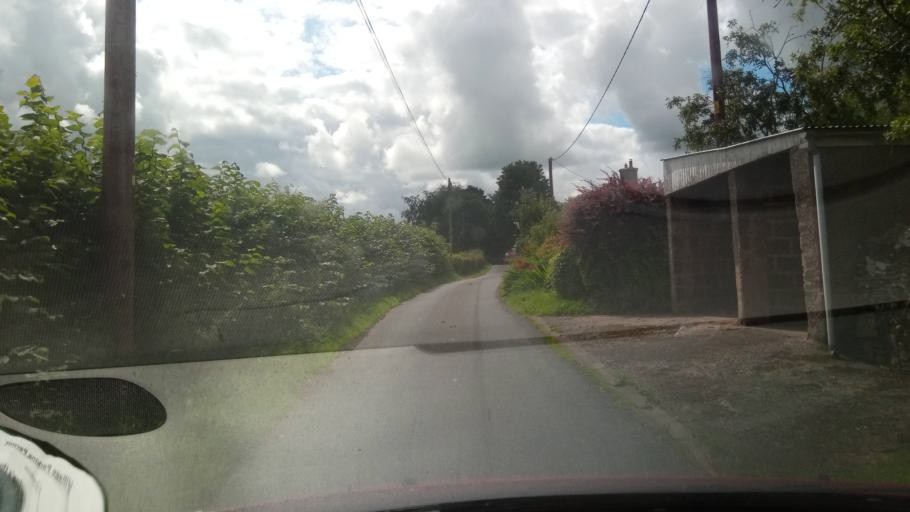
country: GB
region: Scotland
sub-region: The Scottish Borders
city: Hawick
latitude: 55.4177
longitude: -2.7553
